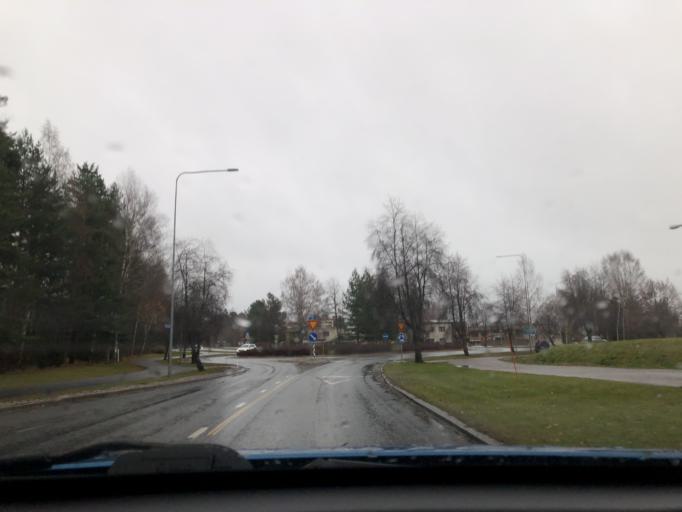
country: FI
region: Pirkanmaa
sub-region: Tampere
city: Kangasala
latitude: 61.4696
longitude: 24.0387
